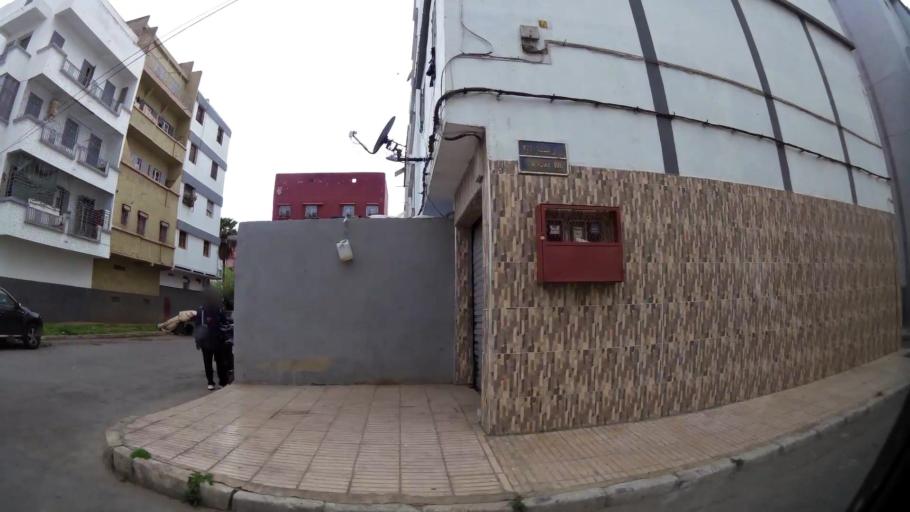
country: MA
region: Grand Casablanca
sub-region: Casablanca
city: Casablanca
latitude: 33.5652
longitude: -7.5595
